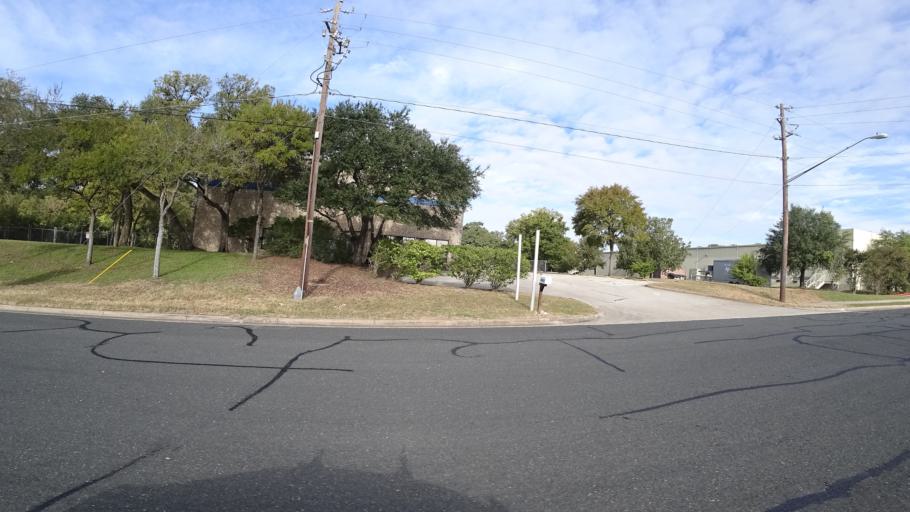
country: US
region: Texas
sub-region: Travis County
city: Austin
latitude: 30.2066
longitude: -97.7292
